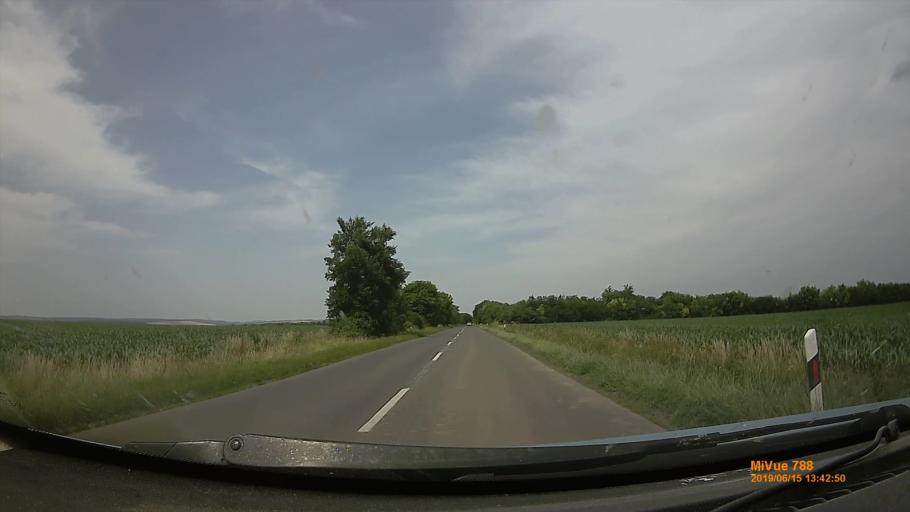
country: HU
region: Tolna
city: Iregszemcse
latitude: 46.6693
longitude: 18.1831
